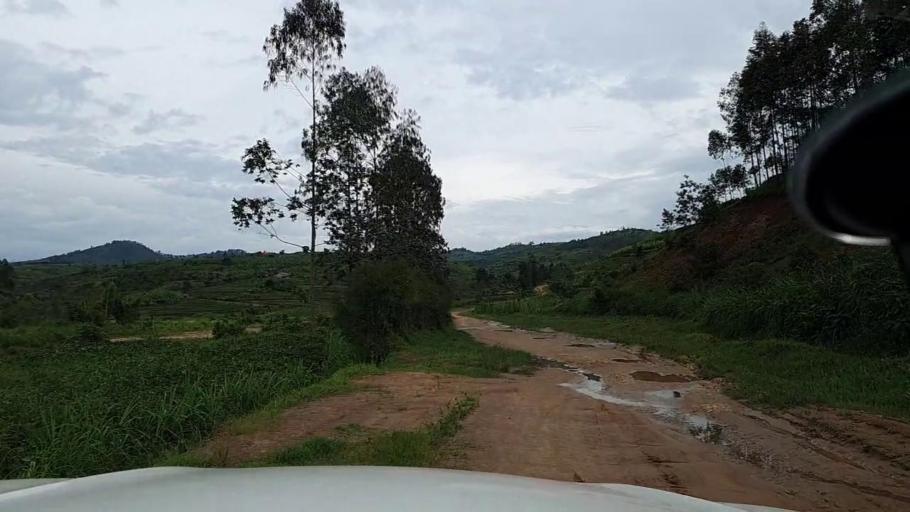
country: RW
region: Southern Province
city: Gitarama
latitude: -2.0968
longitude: 29.6405
